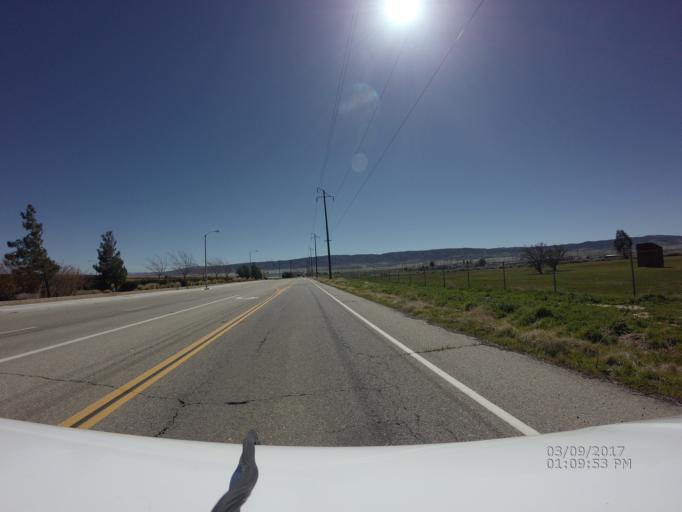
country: US
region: California
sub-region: Los Angeles County
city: Leona Valley
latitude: 34.7017
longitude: -118.2894
